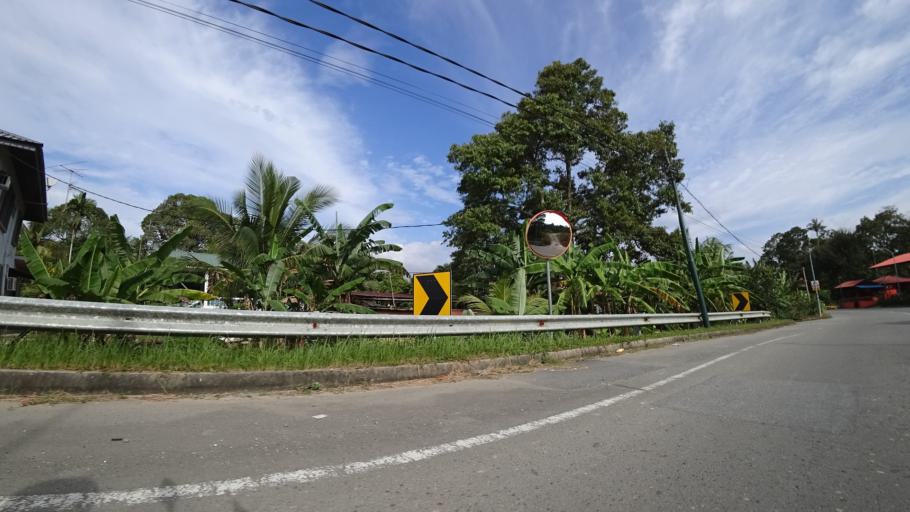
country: BN
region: Brunei and Muara
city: Bandar Seri Begawan
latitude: 4.8693
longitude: 114.8097
